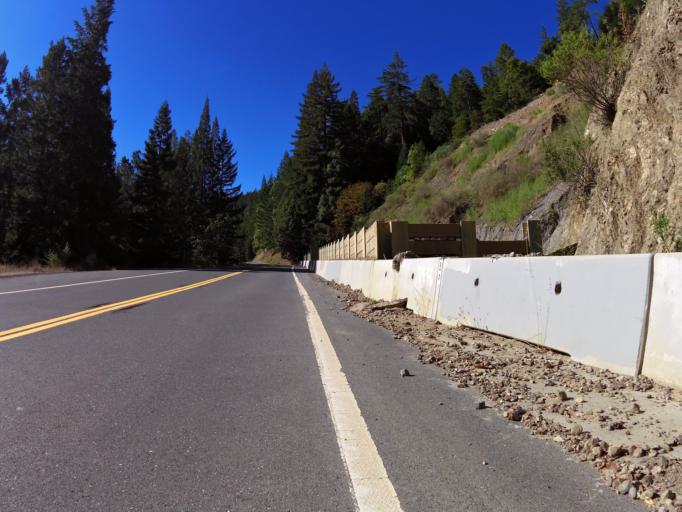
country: US
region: California
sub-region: Humboldt County
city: Redway
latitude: 39.8593
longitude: -123.7283
